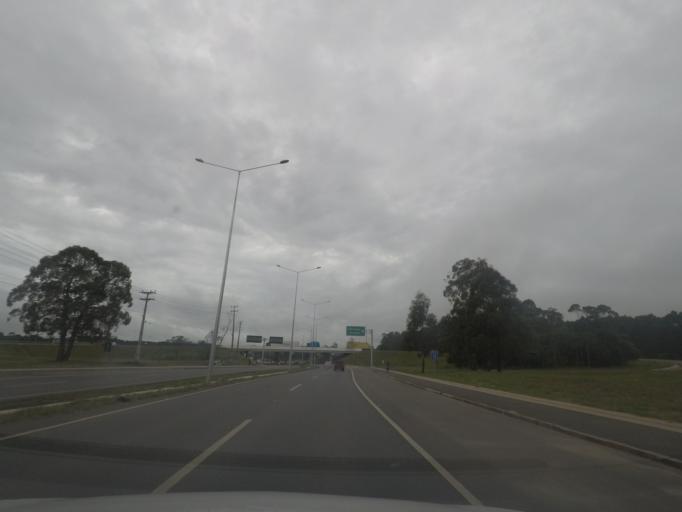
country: BR
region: Parana
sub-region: Piraquara
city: Piraquara
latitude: -25.4614
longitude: -49.0908
